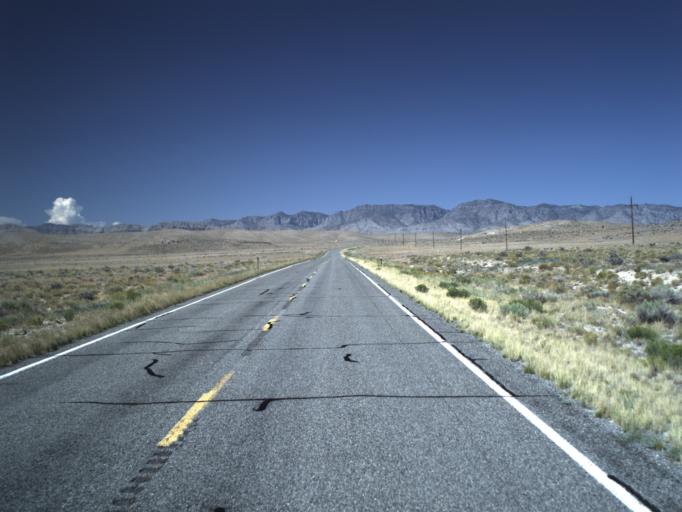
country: US
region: Utah
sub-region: Beaver County
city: Milford
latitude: 39.0433
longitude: -113.2927
